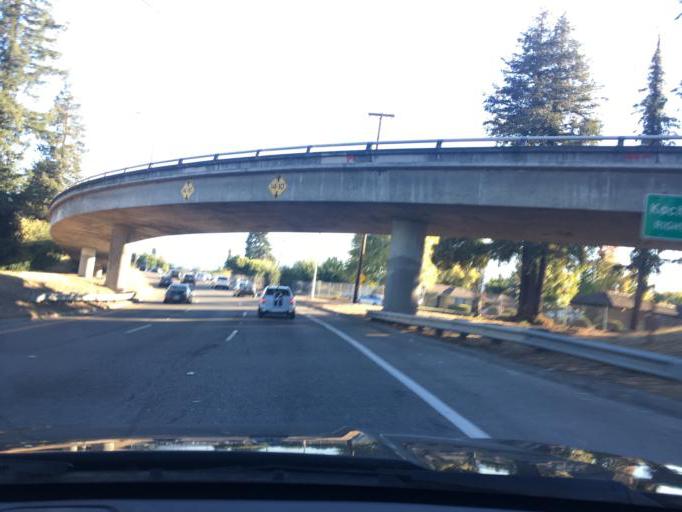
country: US
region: California
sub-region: Santa Clara County
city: Seven Trees
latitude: 37.2858
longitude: -121.8839
